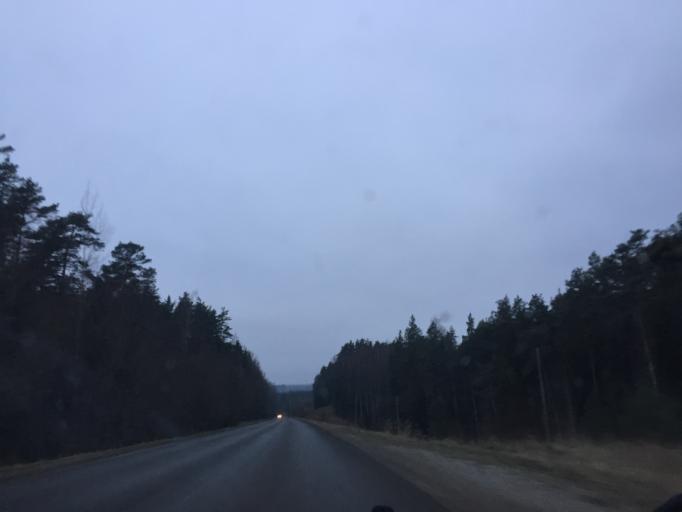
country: LV
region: Priekuli
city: Priekuli
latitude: 57.3262
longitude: 25.4223
